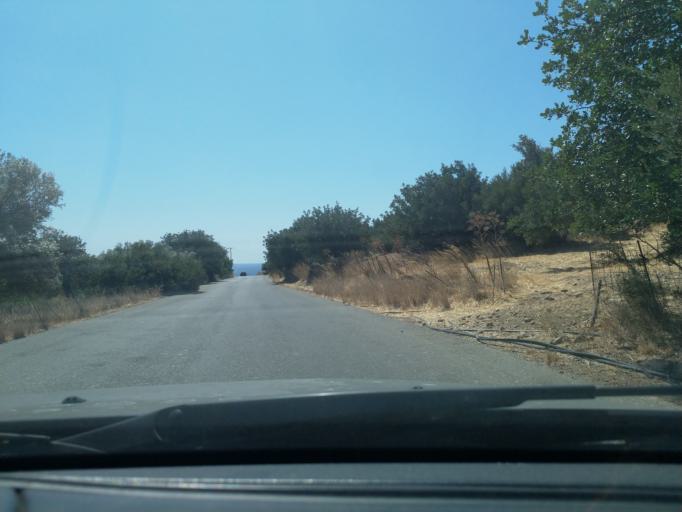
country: GR
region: Crete
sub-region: Nomos Rethymnis
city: Agia Galini
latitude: 35.1227
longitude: 24.5551
